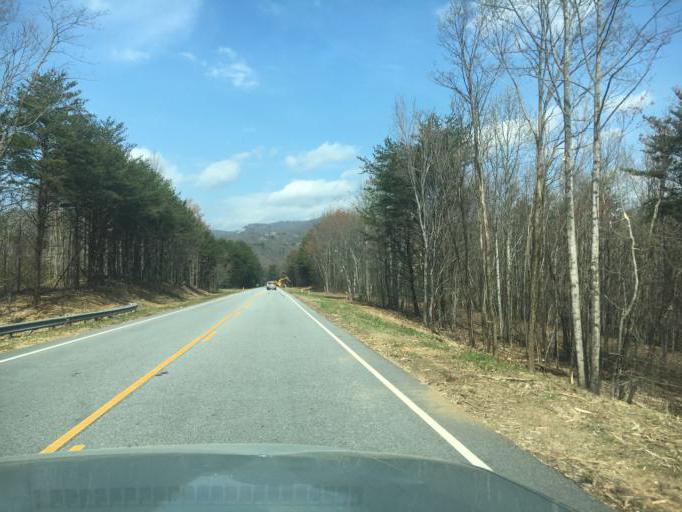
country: US
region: North Carolina
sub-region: Polk County
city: Tryon
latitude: 35.1238
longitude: -82.2870
